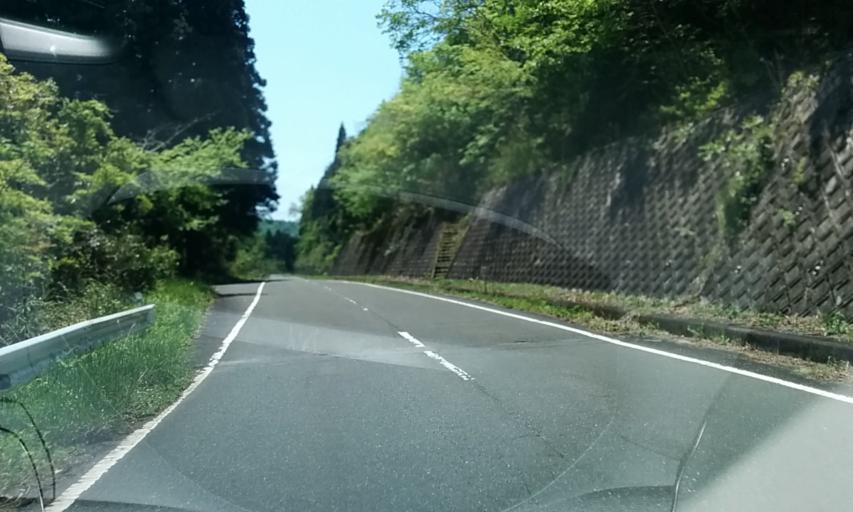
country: JP
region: Kyoto
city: Ayabe
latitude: 35.2163
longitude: 135.2946
